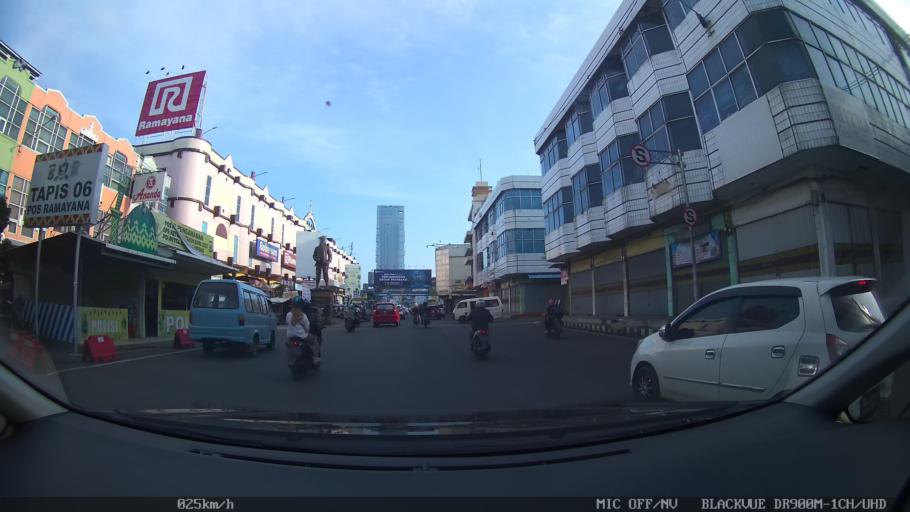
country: ID
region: Lampung
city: Bandarlampung
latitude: -5.4096
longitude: 105.2586
